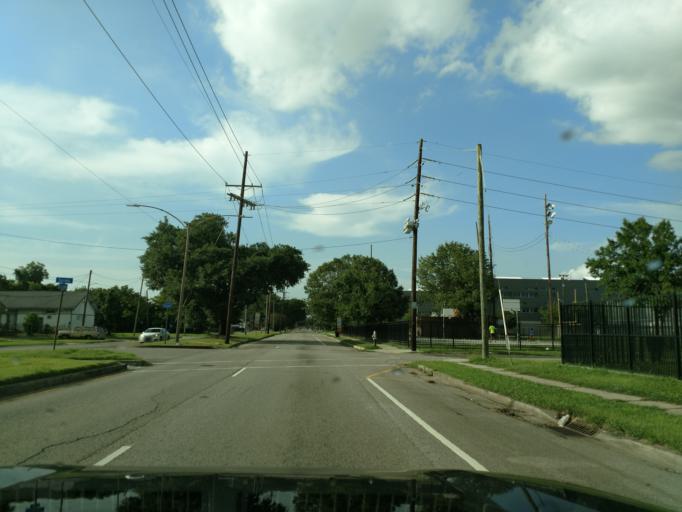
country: US
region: Louisiana
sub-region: Jefferson Parish
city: Gretna
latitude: 29.9407
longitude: -90.0411
